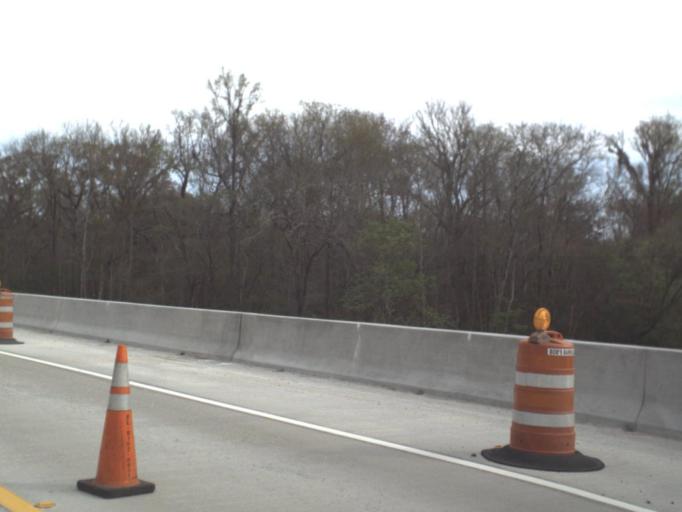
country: US
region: Florida
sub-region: Leon County
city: Woodville
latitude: 30.1464
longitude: -83.9734
